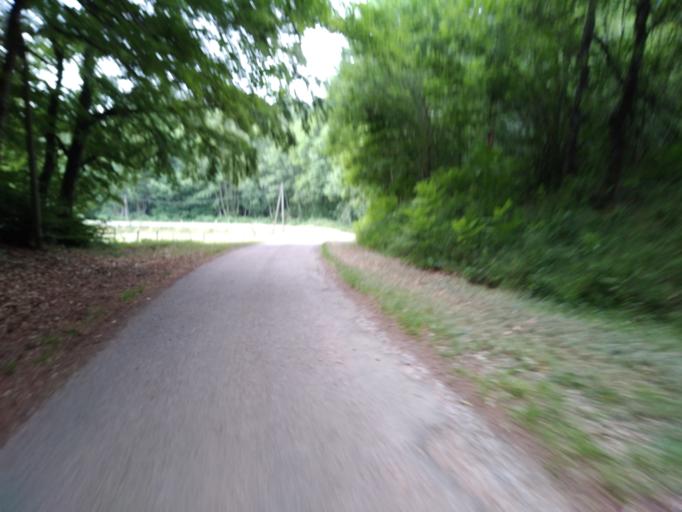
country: FR
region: Bourgogne
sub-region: Departement de la Cote-d'Or
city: Saulieu
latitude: 47.2773
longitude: 4.1222
